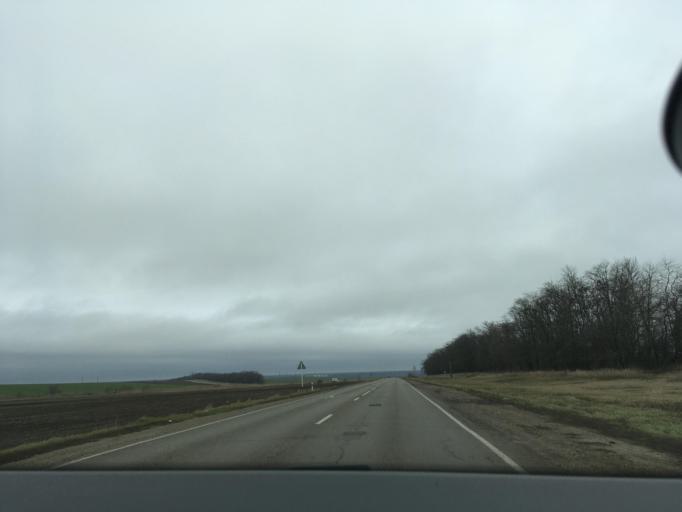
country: RU
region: Krasnodarskiy
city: Kushchevskaya
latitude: 46.6004
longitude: 39.6538
